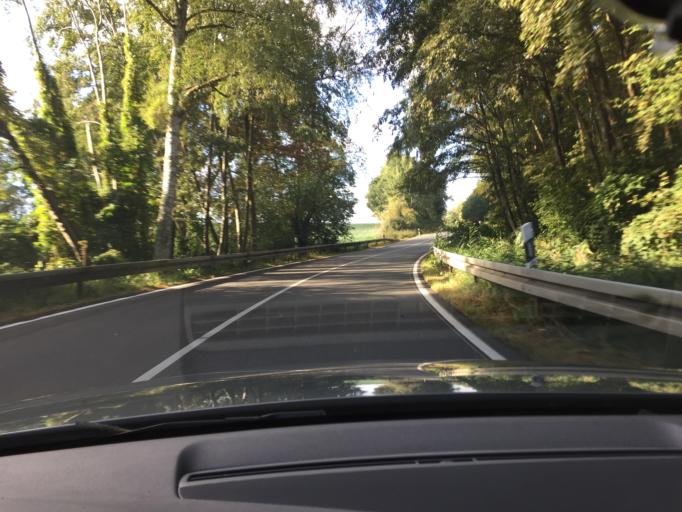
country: DE
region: Mecklenburg-Vorpommern
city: Krakow am See
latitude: 53.6879
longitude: 12.3371
